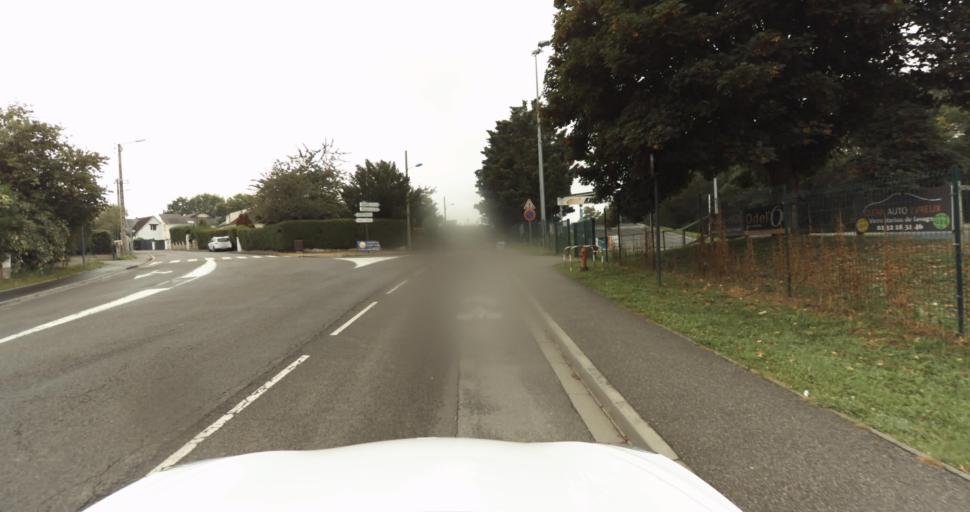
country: FR
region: Haute-Normandie
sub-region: Departement de l'Eure
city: Evreux
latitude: 49.0325
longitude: 1.1415
